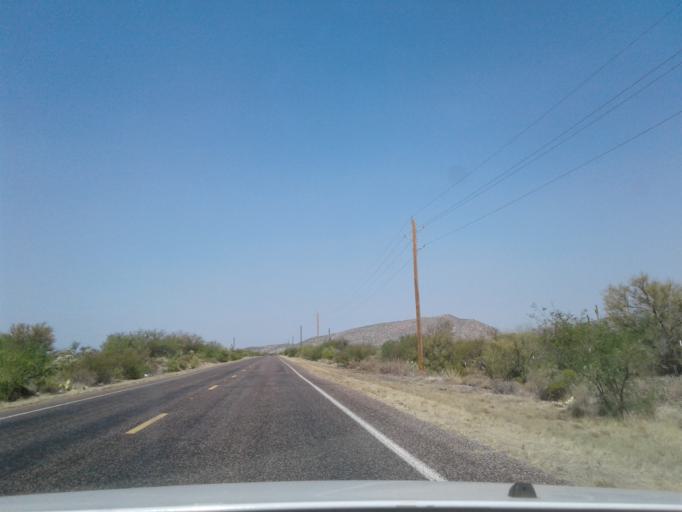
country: US
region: Arizona
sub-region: Pima County
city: Catalina
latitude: 32.6572
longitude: -111.0895
